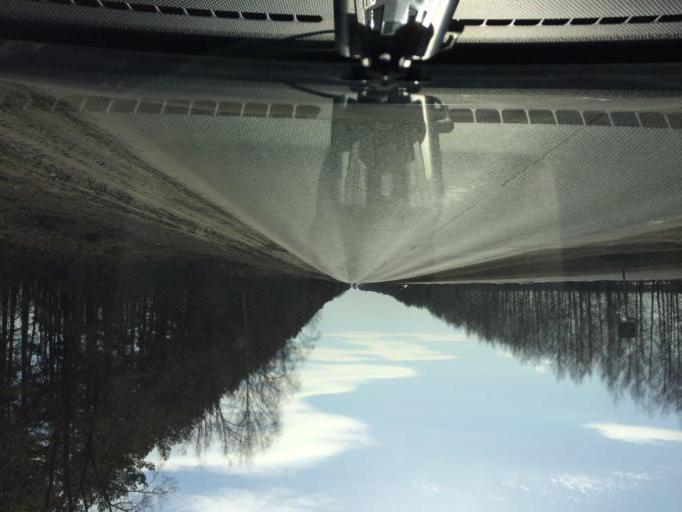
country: RU
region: Mariy-El
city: Surok
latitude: 56.7376
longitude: 48.1730
